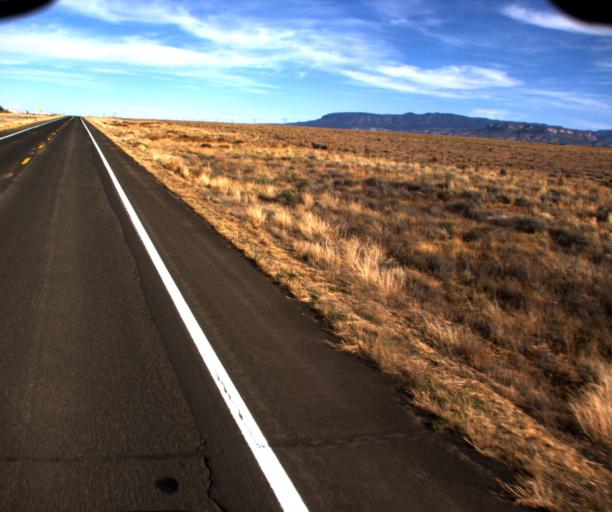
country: US
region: Arizona
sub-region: Apache County
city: Lukachukai
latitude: 36.9611
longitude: -109.3902
